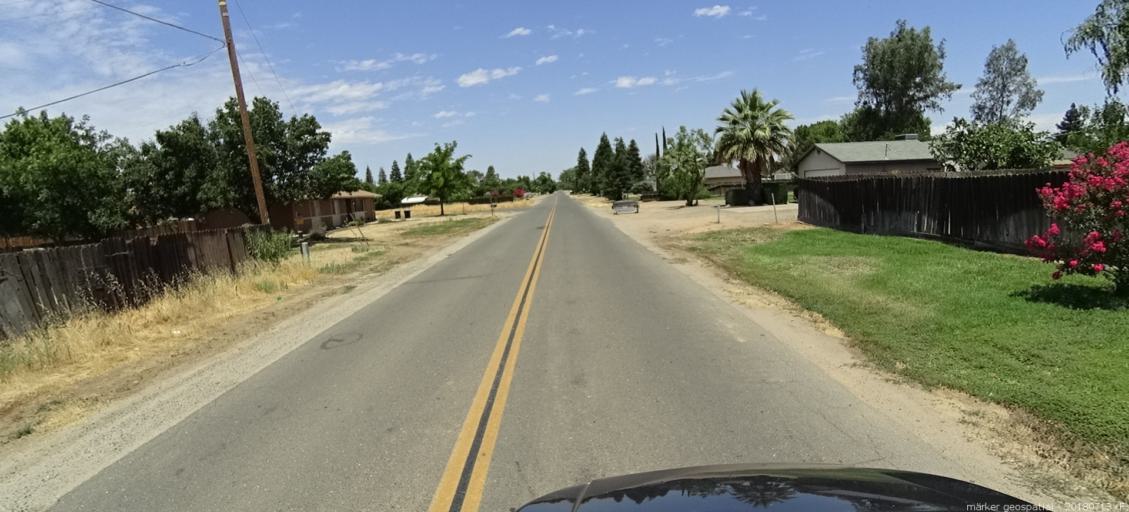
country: US
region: California
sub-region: Madera County
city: Madera Acres
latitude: 36.9930
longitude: -120.0767
